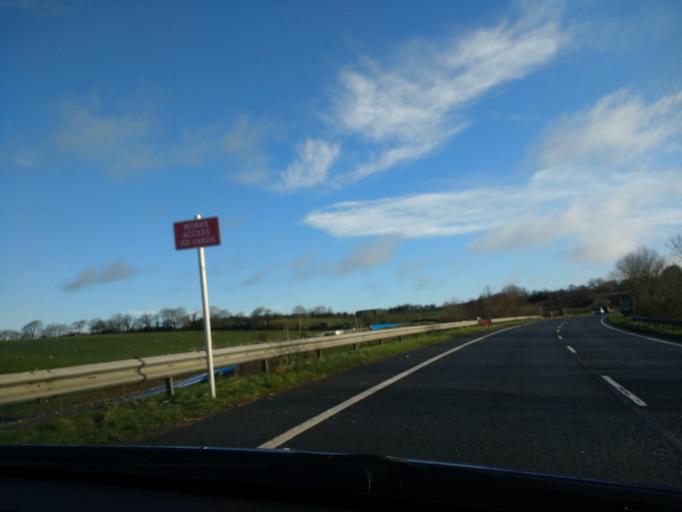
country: GB
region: England
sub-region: Cumbria
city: Cockermouth
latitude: 54.6691
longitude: -3.3918
